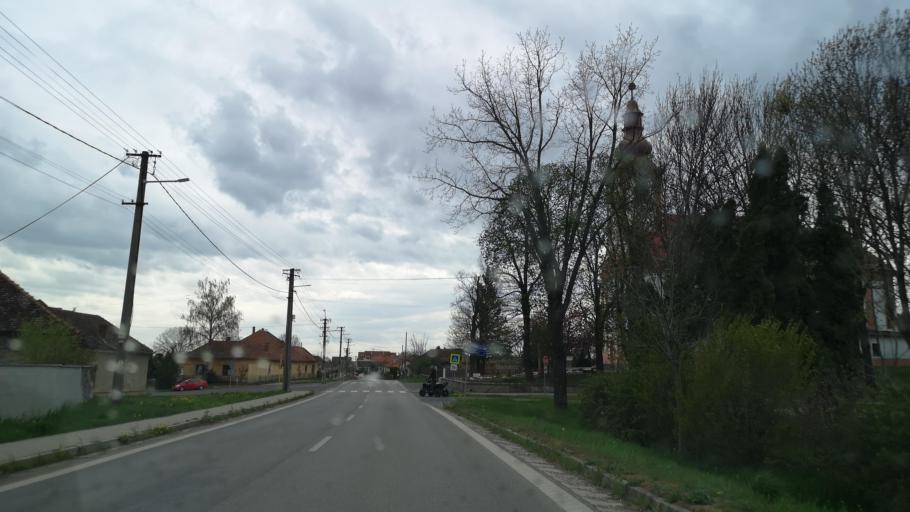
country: SK
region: Nitriansky
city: Zlate Moravce
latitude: 48.3401
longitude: 18.3580
